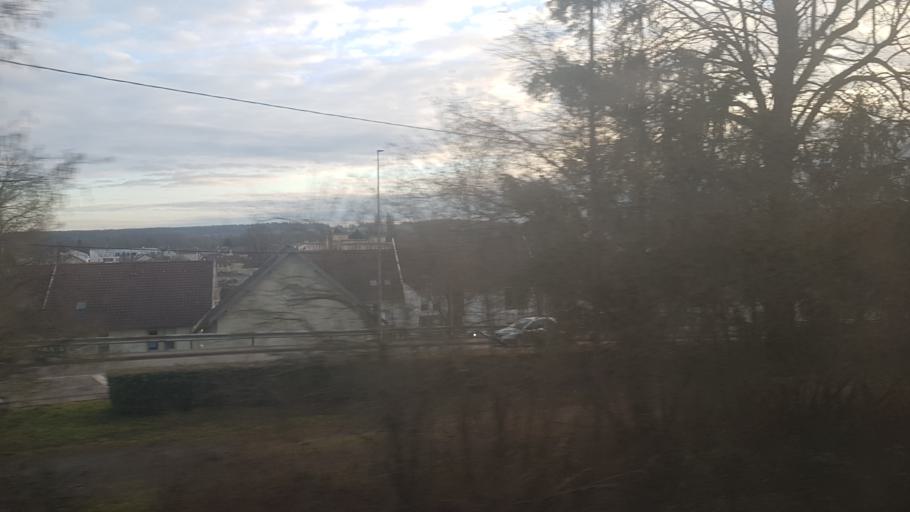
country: FR
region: Lorraine
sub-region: Departement des Vosges
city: Thaon-les-Vosges
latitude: 48.2538
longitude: 6.4095
